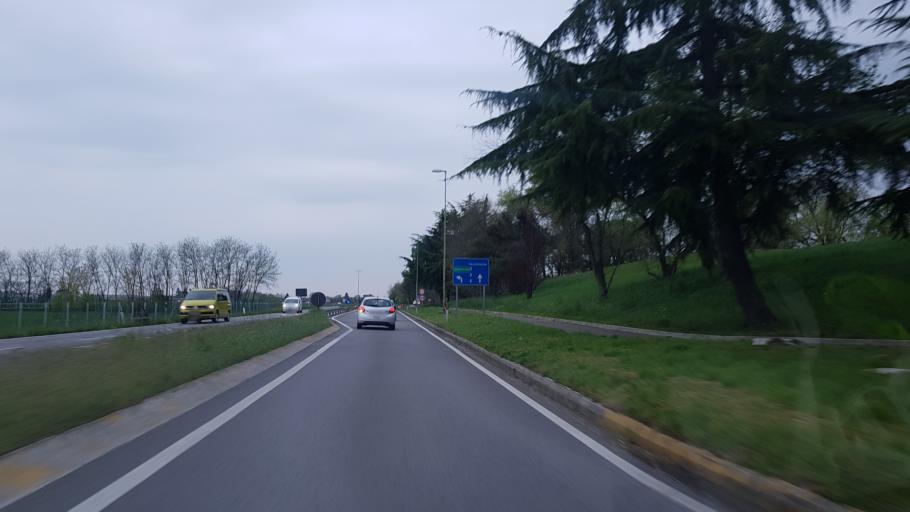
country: IT
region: Friuli Venezia Giulia
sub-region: Provincia di Udine
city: Visco
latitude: 45.8911
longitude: 13.3606
